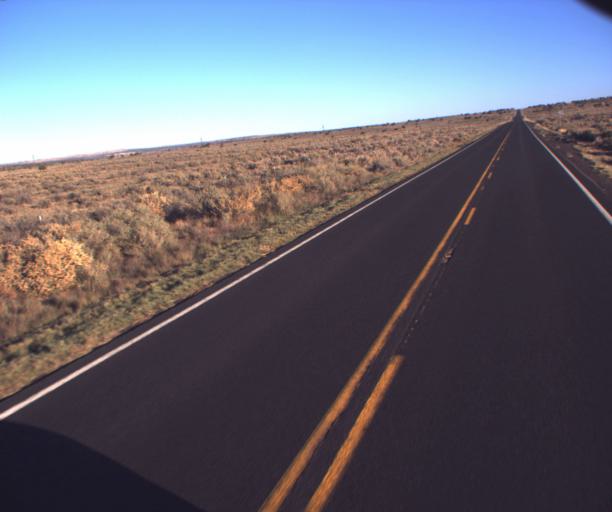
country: US
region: Arizona
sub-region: Apache County
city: Houck
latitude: 35.2046
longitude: -109.4394
